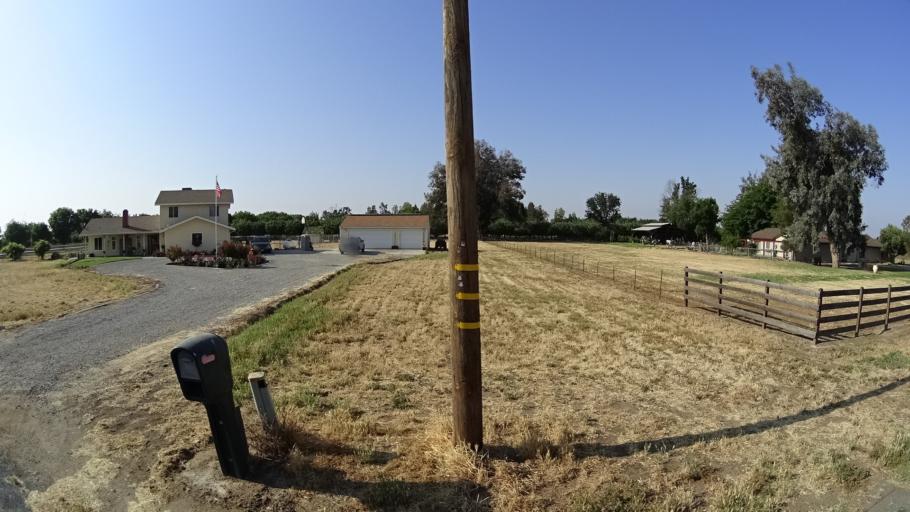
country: US
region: California
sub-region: Kings County
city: Lemoore
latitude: 36.3584
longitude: -119.8262
